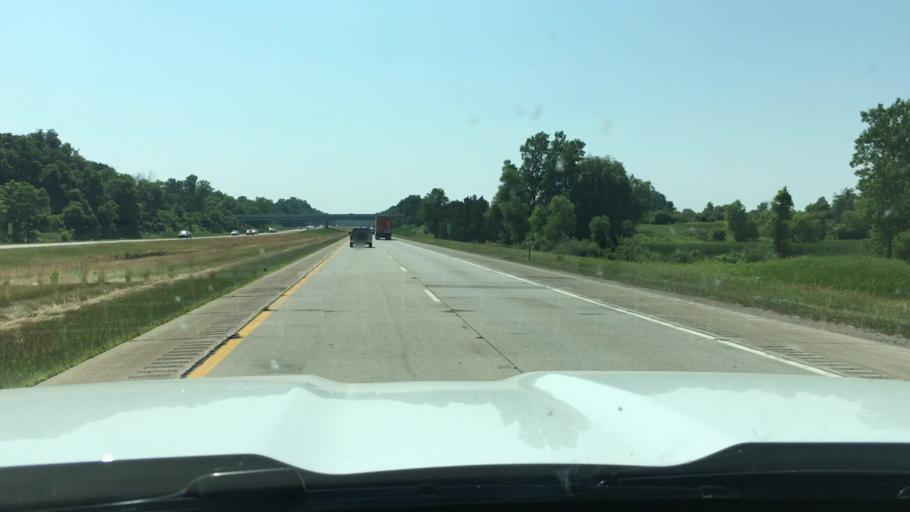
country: US
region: Michigan
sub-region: Clinton County
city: DeWitt
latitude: 42.8078
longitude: -84.5976
